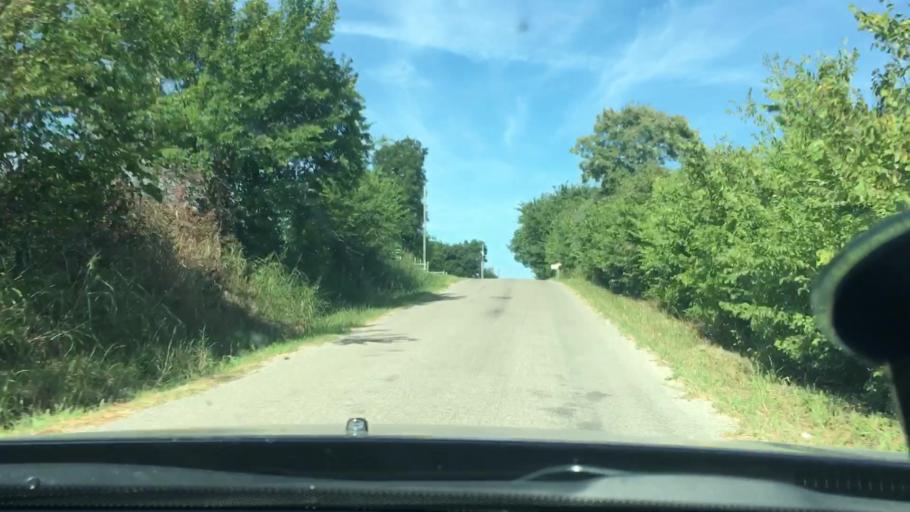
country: US
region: Oklahoma
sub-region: Carter County
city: Lone Grove
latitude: 34.2674
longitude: -97.2620
